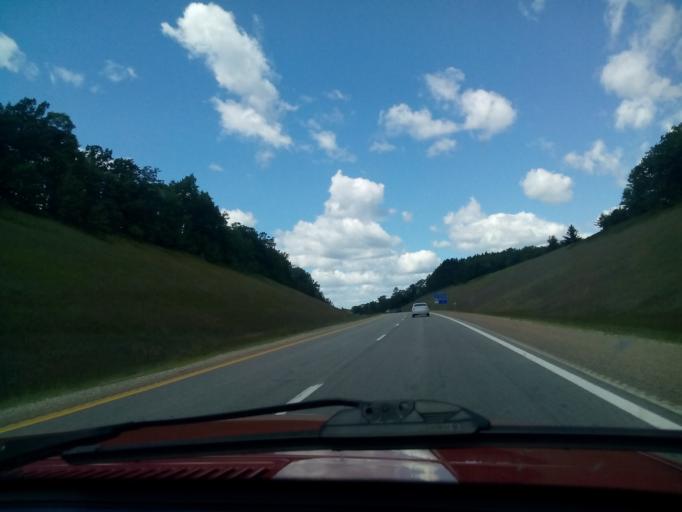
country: US
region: Michigan
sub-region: Roscommon County
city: Roscommon
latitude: 44.4463
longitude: -84.5953
